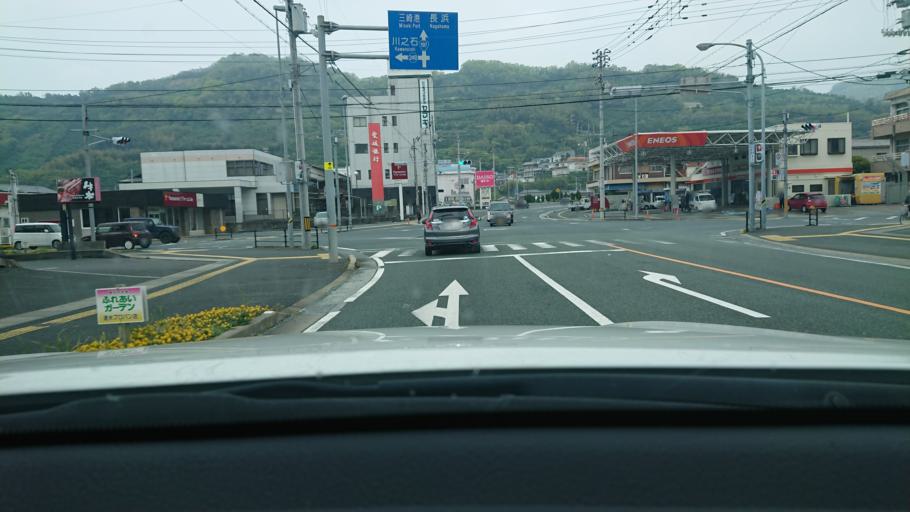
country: JP
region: Ehime
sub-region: Nishiuwa-gun
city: Ikata-cho
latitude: 33.4842
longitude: 132.4007
